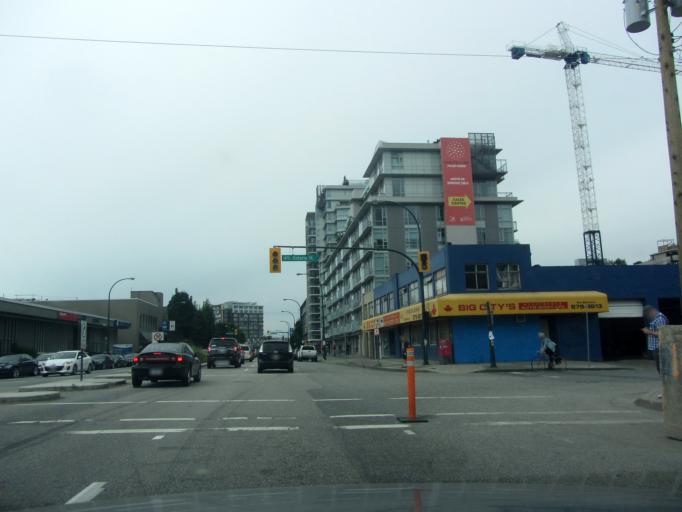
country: CA
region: British Columbia
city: Vancouver
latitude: 49.2619
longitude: -123.0982
